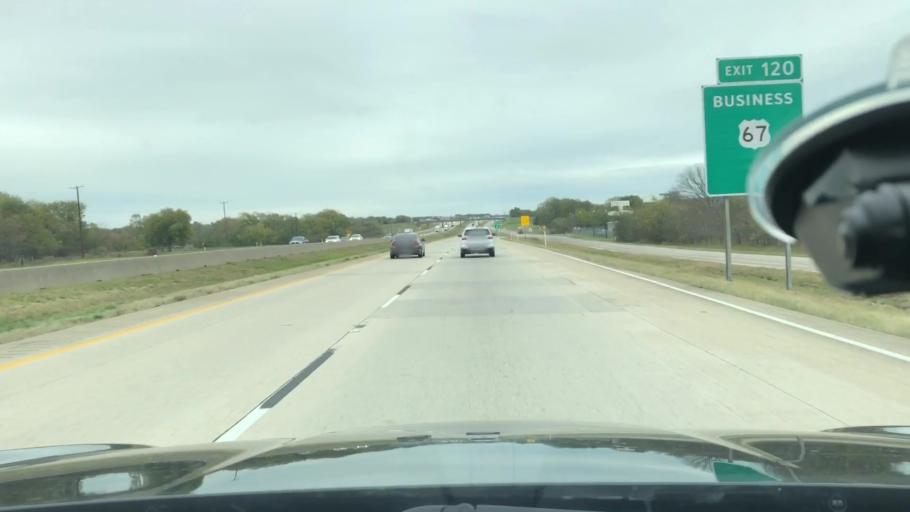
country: US
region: Texas
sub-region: Hopkins County
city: Sulphur Springs
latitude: 33.1208
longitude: -95.6802
